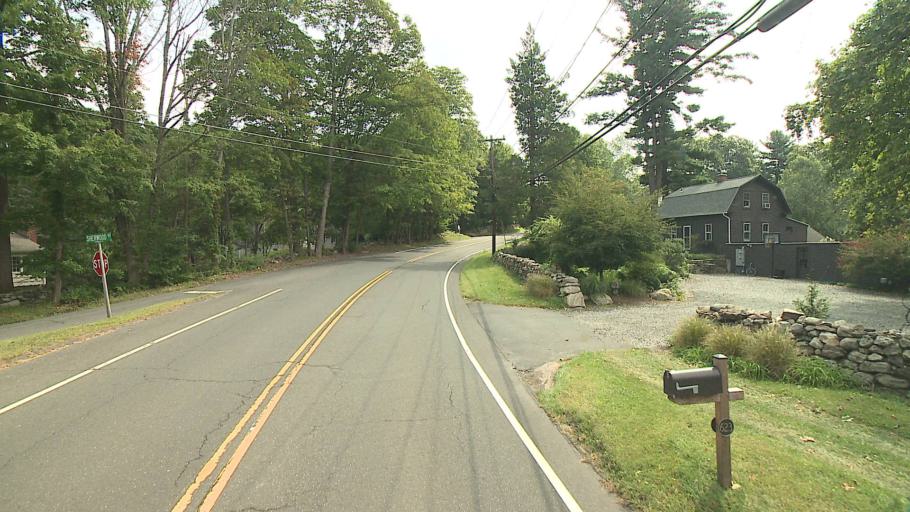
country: US
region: Connecticut
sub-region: Fairfield County
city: Ridgefield
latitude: 41.3231
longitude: -73.5223
